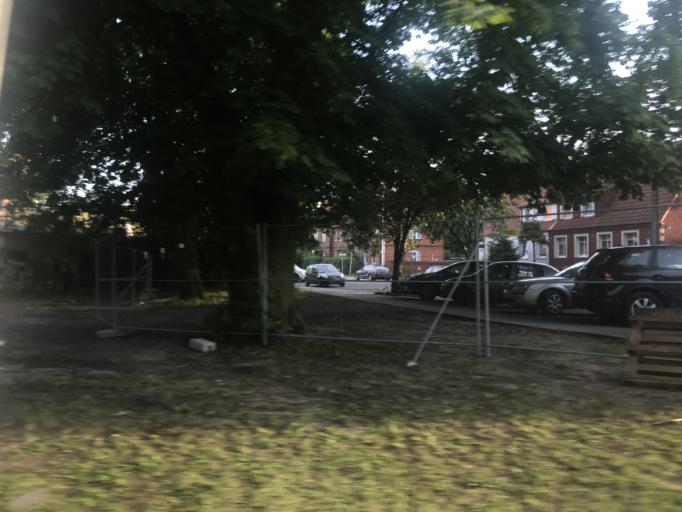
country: PL
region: Pomeranian Voivodeship
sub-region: Gdansk
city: Gdansk
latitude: 54.4076
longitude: 18.6368
